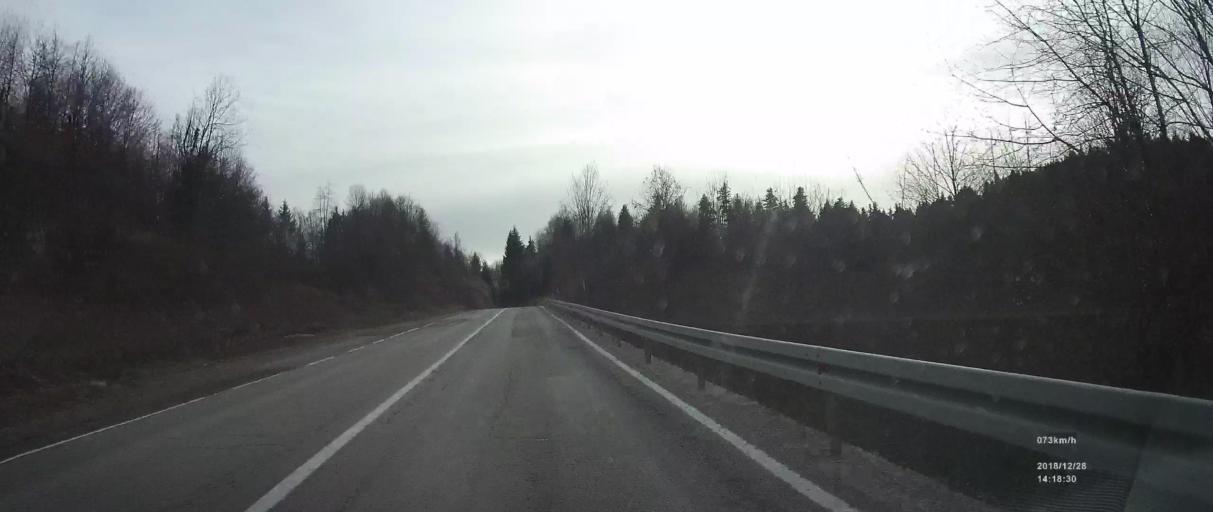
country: HR
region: Primorsko-Goranska
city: Vrbovsko
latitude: 45.4122
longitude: 15.0600
